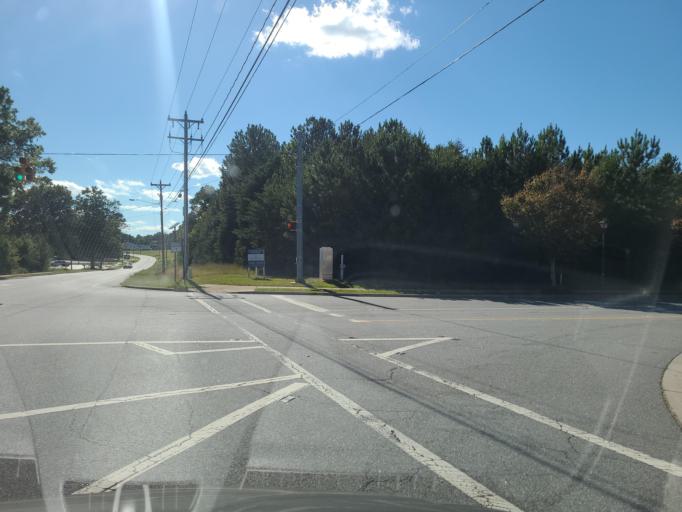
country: US
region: North Carolina
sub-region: Catawba County
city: Conover
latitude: 35.7245
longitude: -81.2106
